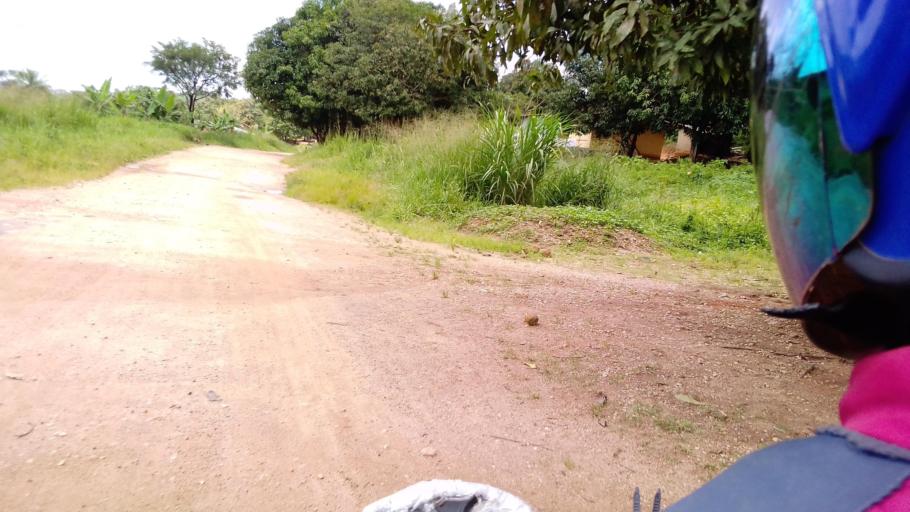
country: SL
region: Eastern Province
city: Koyima
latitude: 8.6938
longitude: -11.0105
